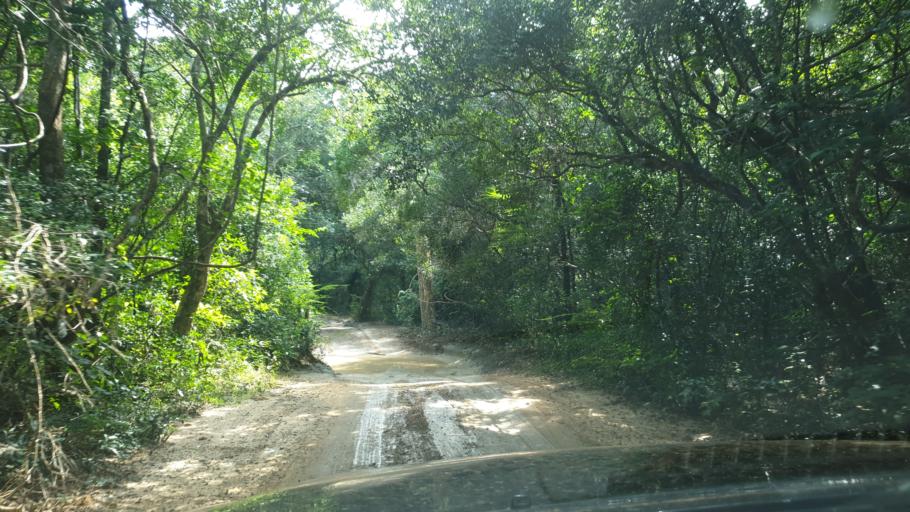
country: LK
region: North Central
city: Anuradhapura
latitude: 8.4181
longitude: 80.0244
